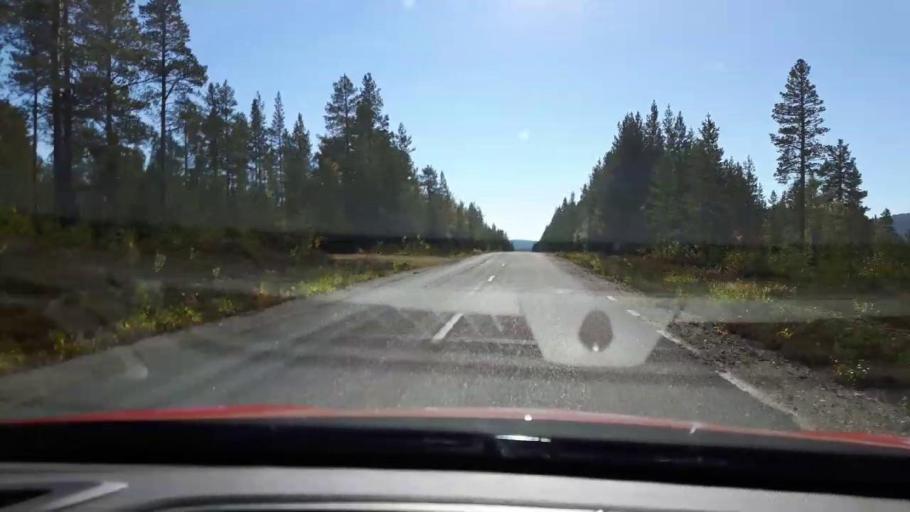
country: SE
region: Jaemtland
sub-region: Harjedalens Kommun
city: Sveg
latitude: 61.7296
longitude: 14.1652
